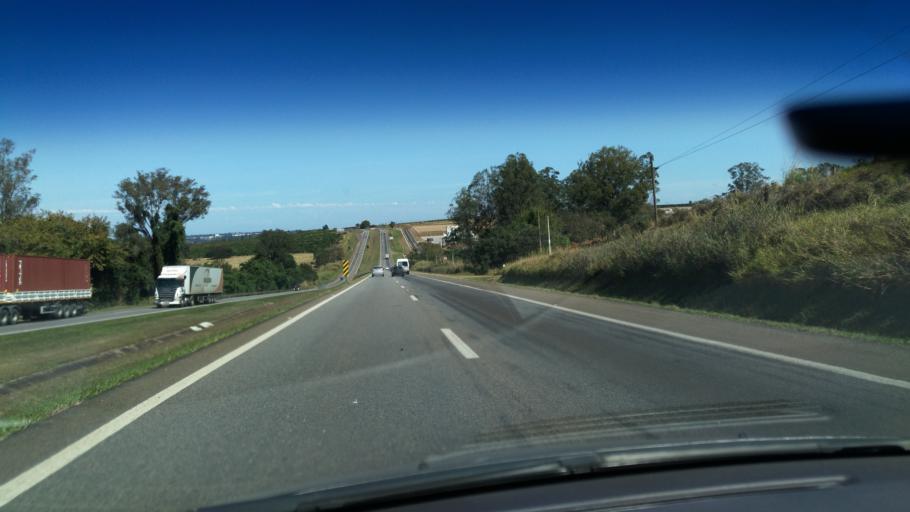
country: BR
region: Sao Paulo
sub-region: Santo Antonio De Posse
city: Santo Antonio de Posse
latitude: -22.5364
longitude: -46.9957
